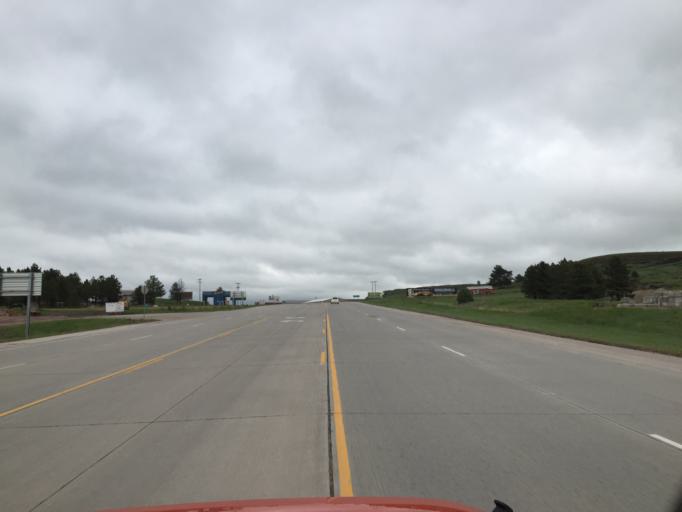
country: US
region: South Dakota
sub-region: Fall River County
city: Hot Springs
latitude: 43.4004
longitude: -103.3965
